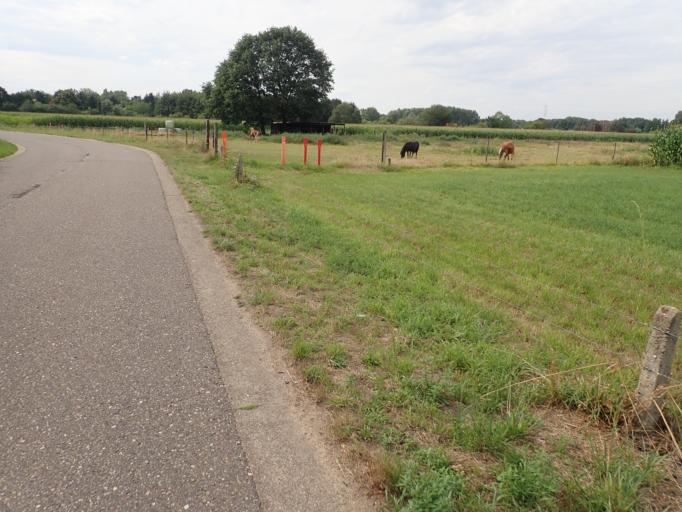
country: BE
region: Flanders
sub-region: Provincie Antwerpen
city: Wommelgem
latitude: 51.2111
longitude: 4.5469
